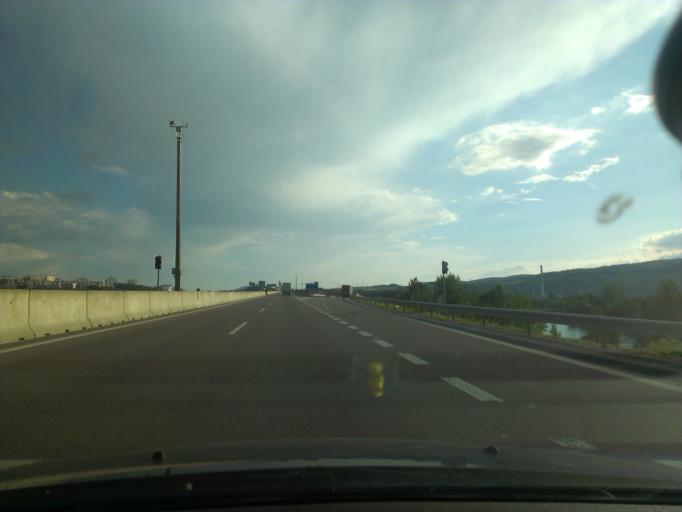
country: SK
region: Trenciansky
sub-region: Okres Povazska Bystrica
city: Povazska Bystrica
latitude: 49.1274
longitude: 18.4504
